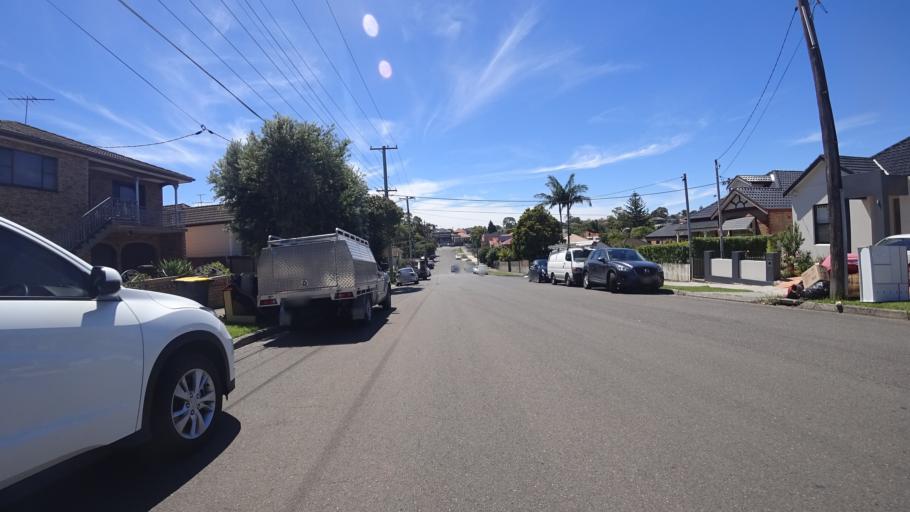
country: AU
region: New South Wales
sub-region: Rockdale
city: Bexley
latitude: -33.9589
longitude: 151.1239
